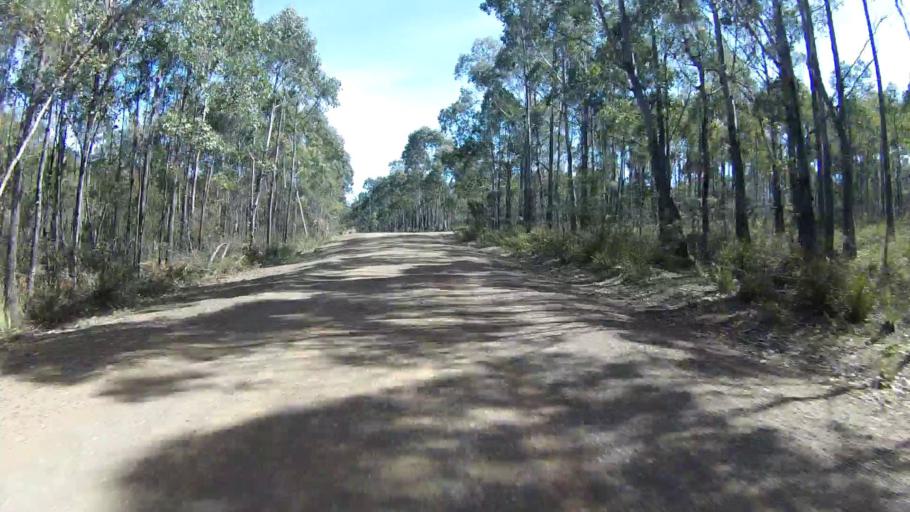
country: AU
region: Tasmania
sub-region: Sorell
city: Sorell
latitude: -42.6786
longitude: 147.7310
